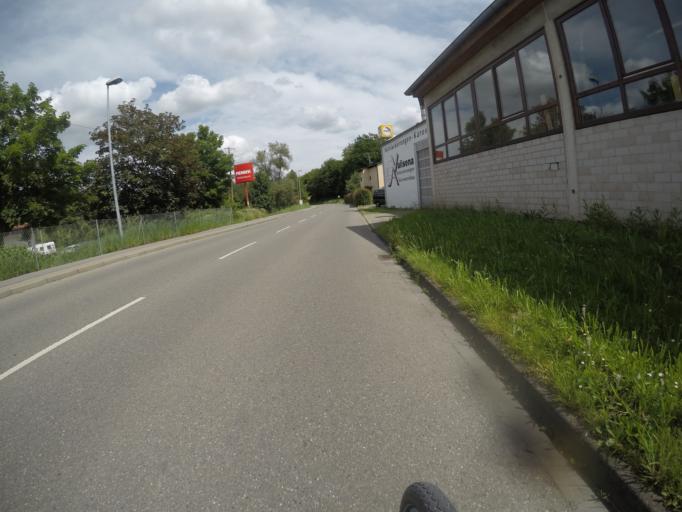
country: DE
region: Baden-Wuerttemberg
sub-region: Regierungsbezirk Stuttgart
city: Waldenbuch
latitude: 48.6353
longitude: 9.1444
